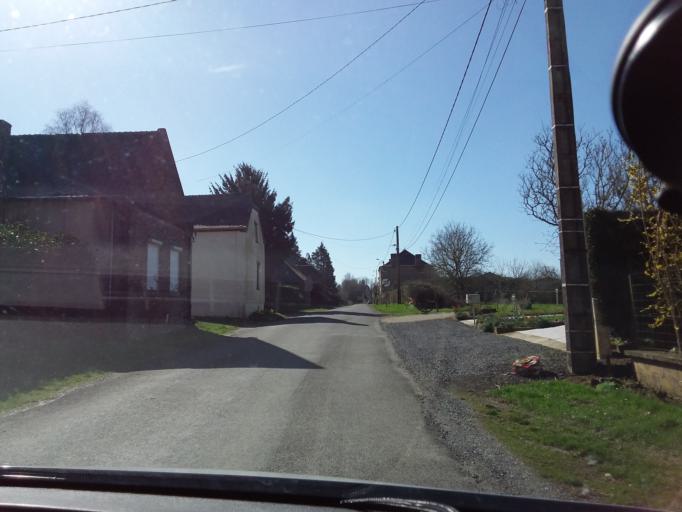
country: FR
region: Picardie
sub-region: Departement de l'Aisne
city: Montcornet
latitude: 49.7535
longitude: 4.0013
